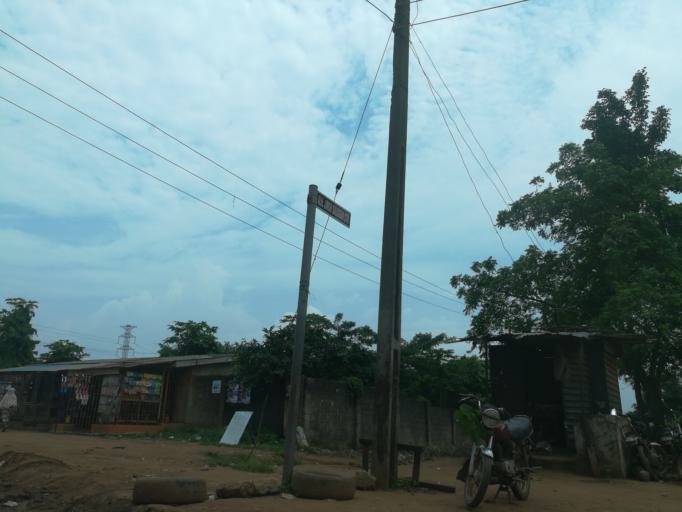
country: NG
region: Lagos
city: Ikorodu
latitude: 6.5832
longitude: 3.5948
